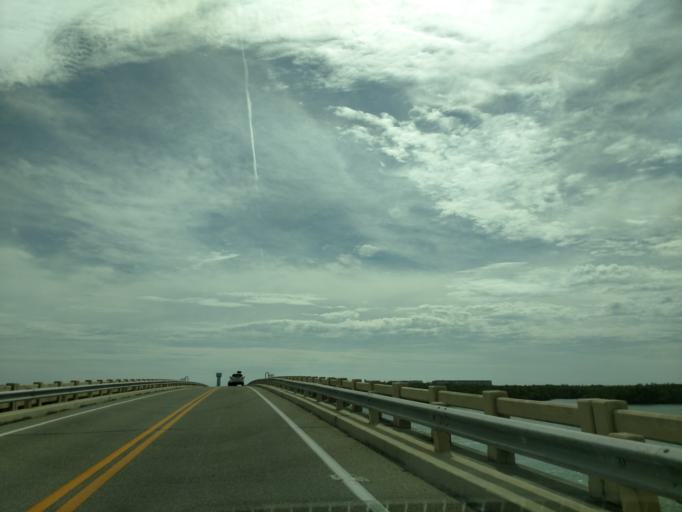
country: US
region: Florida
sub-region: Lee County
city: Estero
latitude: 26.3787
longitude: -81.8613
